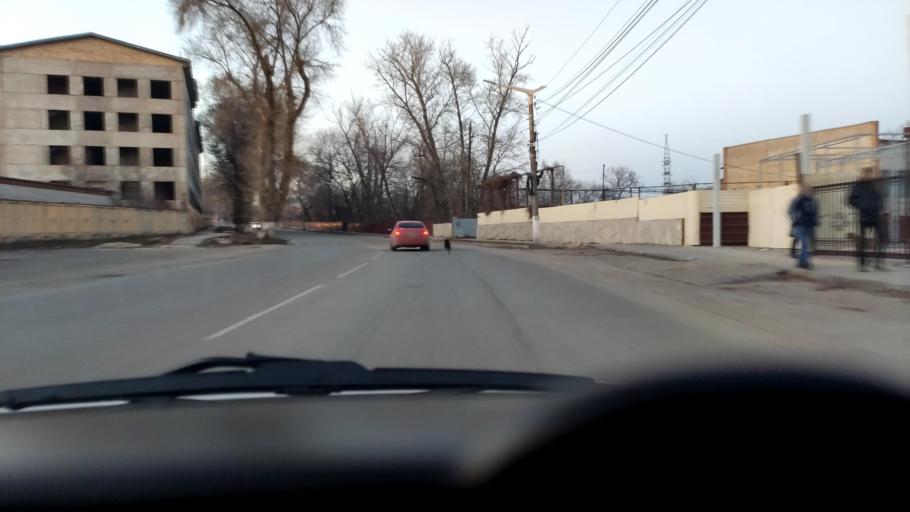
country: RU
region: Voronezj
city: Semiluki
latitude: 51.6889
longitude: 39.0385
